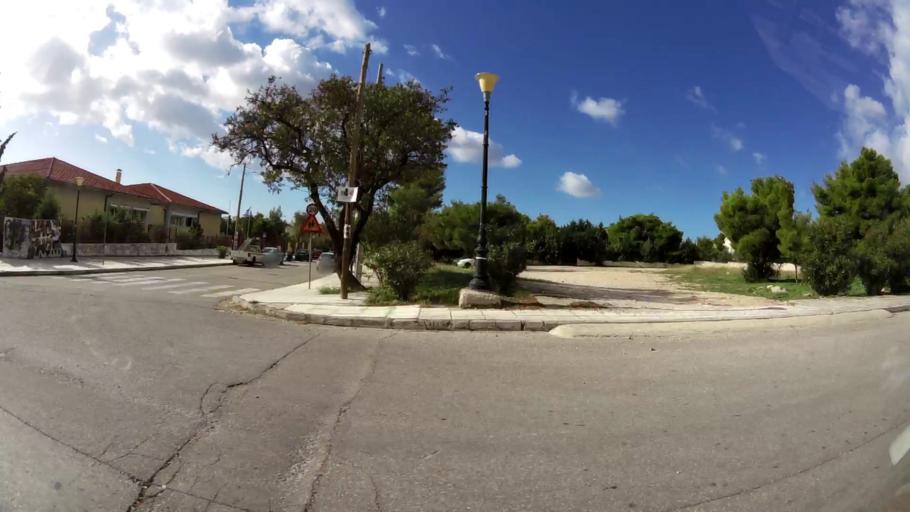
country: GR
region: Attica
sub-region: Nomarchia Anatolikis Attikis
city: Thrakomakedones
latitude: 38.1290
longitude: 23.7568
